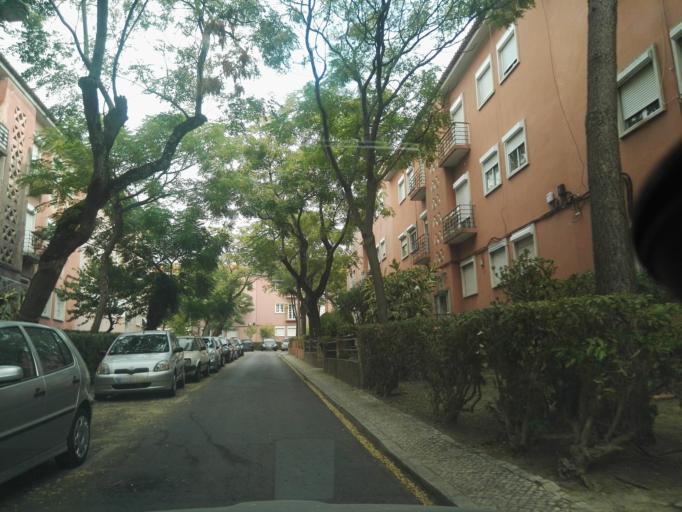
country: PT
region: Lisbon
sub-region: Lisbon
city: Lisbon
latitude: 38.7523
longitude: -9.1477
